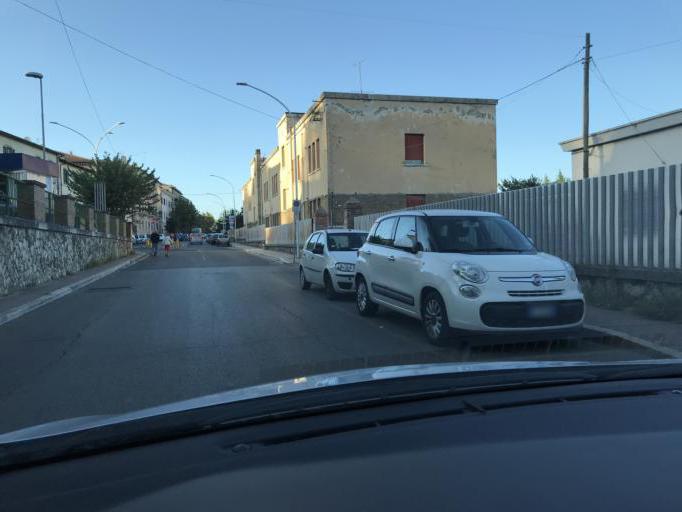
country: IT
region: Latium
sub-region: Provincia di Viterbo
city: Orte Scalo
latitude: 42.4387
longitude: 12.4082
